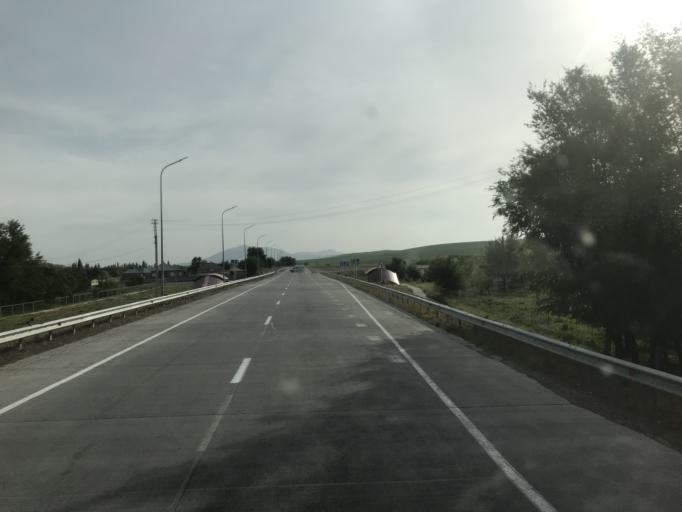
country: KZ
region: Ongtustik Qazaqstan
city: Qazyqurt
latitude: 41.8993
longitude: 69.4581
